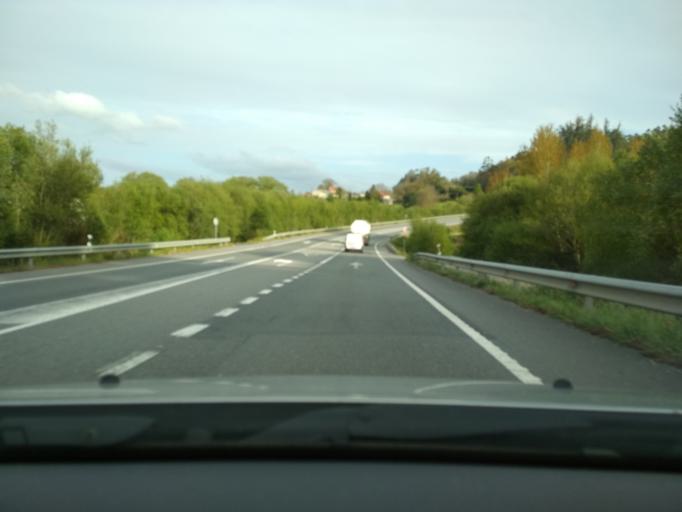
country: ES
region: Galicia
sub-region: Provincia da Coruna
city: Cerceda
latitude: 43.2187
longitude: -8.4572
